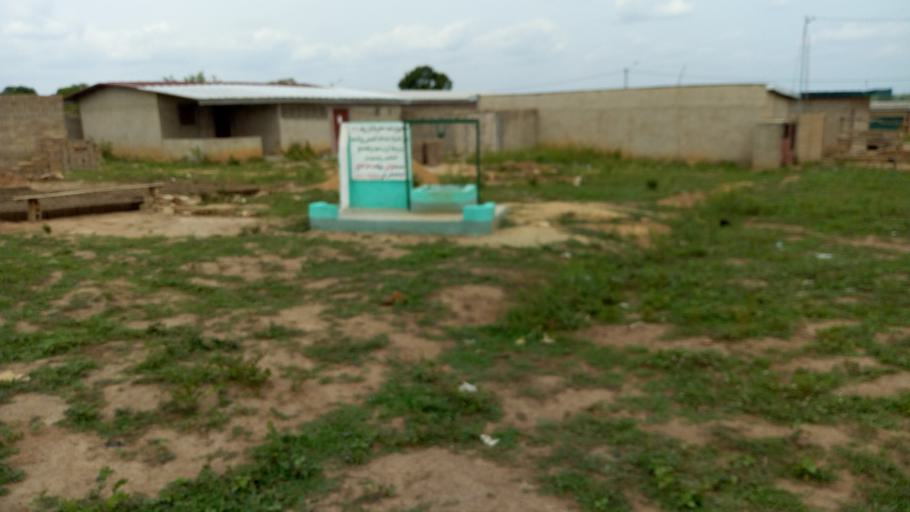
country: CI
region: Vallee du Bandama
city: Bouake
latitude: 7.7129
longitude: -4.9888
